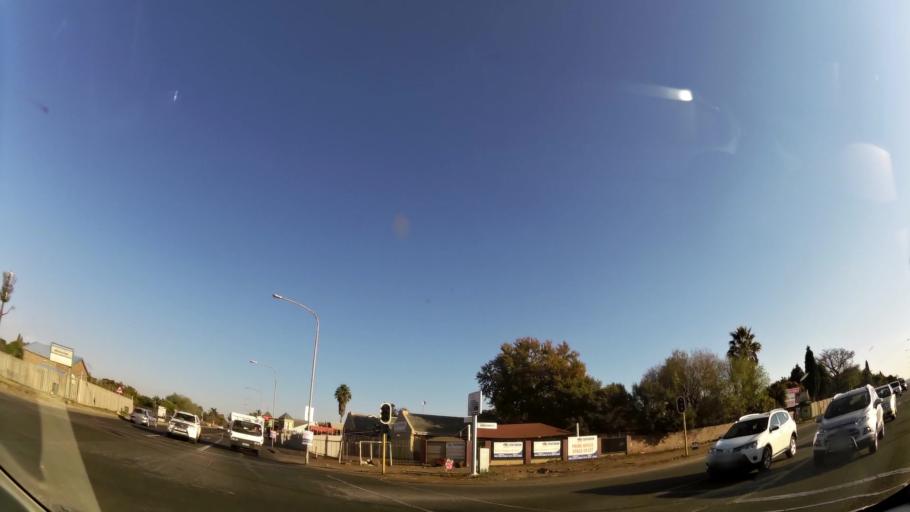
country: ZA
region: Gauteng
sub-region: City of Tshwane Metropolitan Municipality
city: Centurion
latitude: -25.8680
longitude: 28.1517
